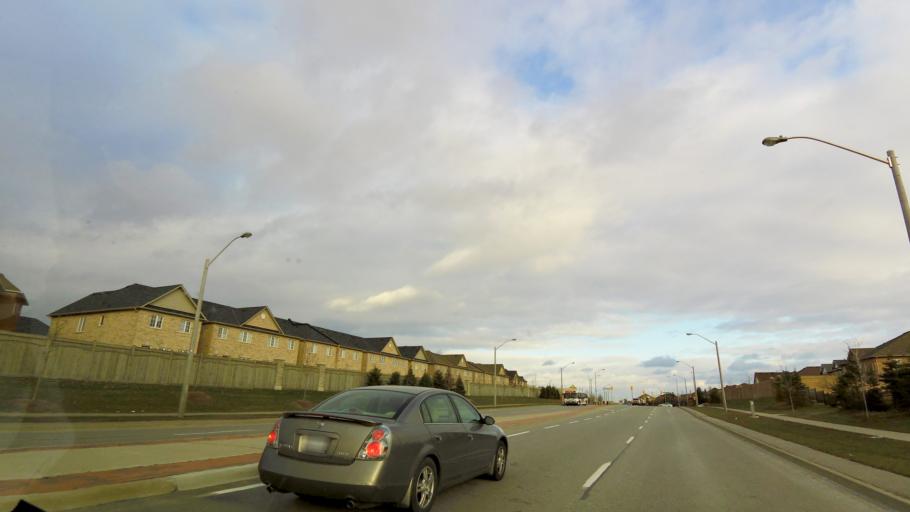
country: CA
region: Ontario
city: Brampton
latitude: 43.7837
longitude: -79.6659
